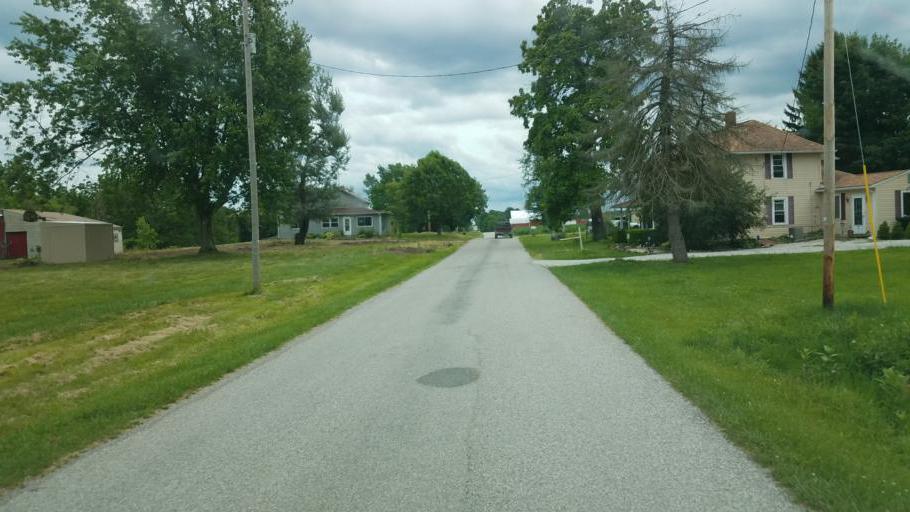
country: US
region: Ohio
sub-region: Licking County
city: Utica
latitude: 40.2047
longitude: -82.5478
